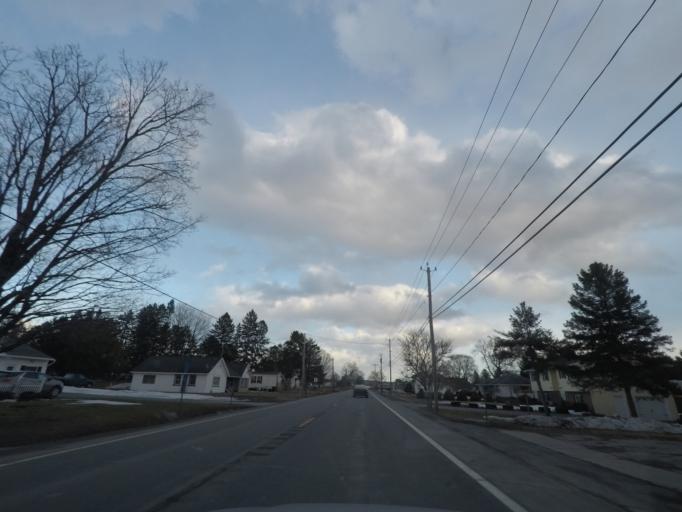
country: US
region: New York
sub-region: Herkimer County
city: Frankfort
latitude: 43.0935
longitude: -75.1385
